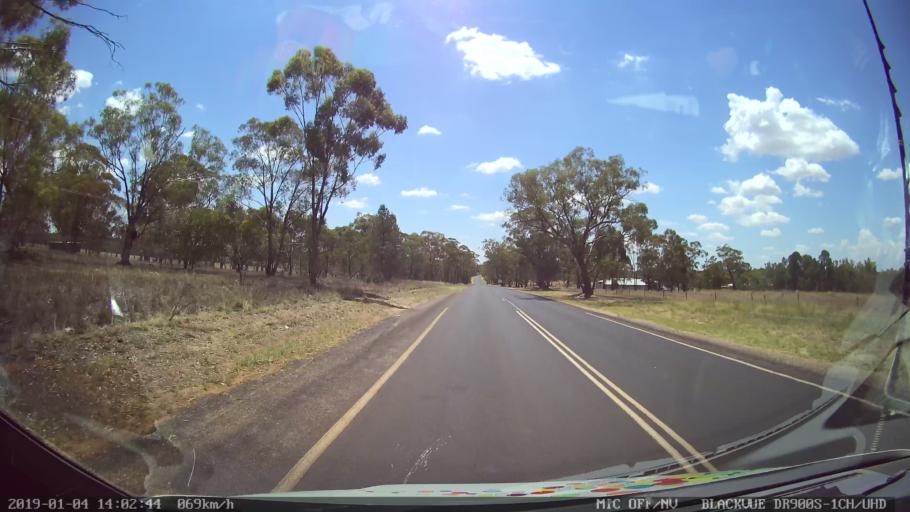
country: AU
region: New South Wales
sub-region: Dubbo Municipality
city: Dubbo
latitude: -32.2838
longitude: 148.5959
